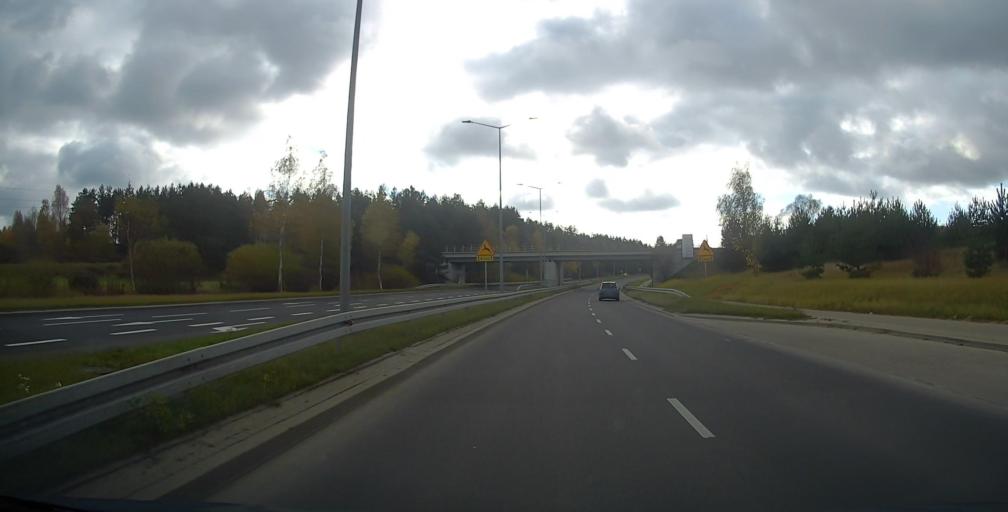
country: PL
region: Warmian-Masurian Voivodeship
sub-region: Powiat elcki
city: Elk
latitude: 53.8188
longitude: 22.3882
